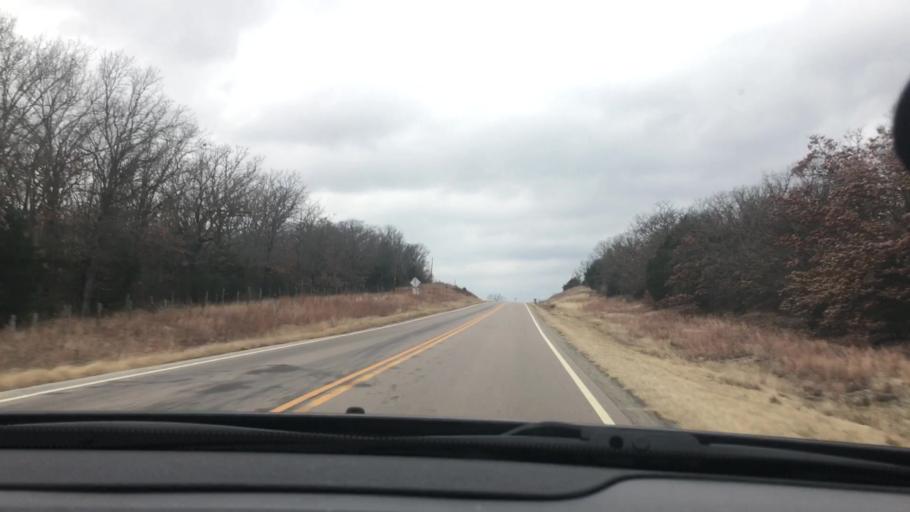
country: US
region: Oklahoma
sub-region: Coal County
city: Coalgate
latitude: 34.3749
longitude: -96.3944
